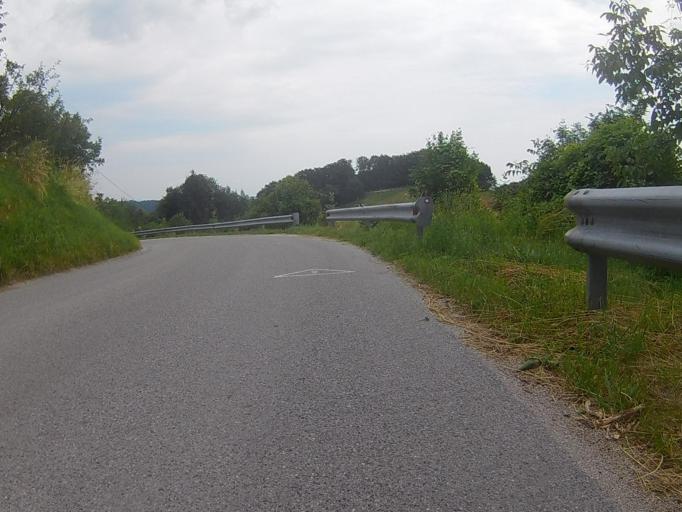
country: SI
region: Sentilj
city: Sentilj v Slov. Goricah
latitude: 46.6726
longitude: 15.6328
